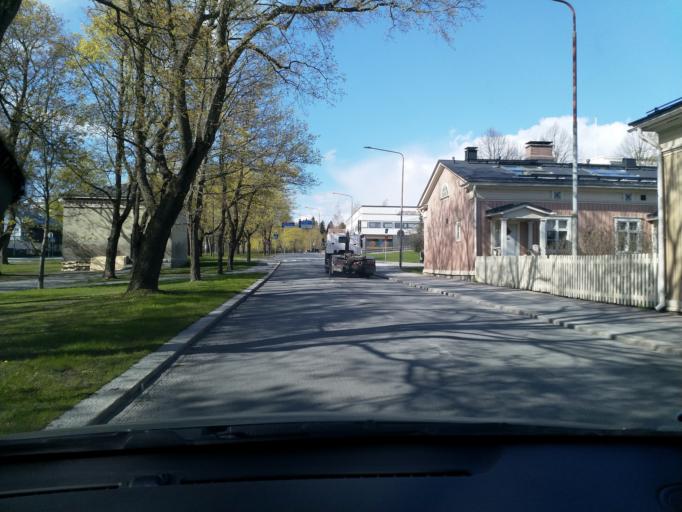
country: FI
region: Pirkanmaa
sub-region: Tampere
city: Tampere
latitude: 61.5037
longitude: 23.7870
